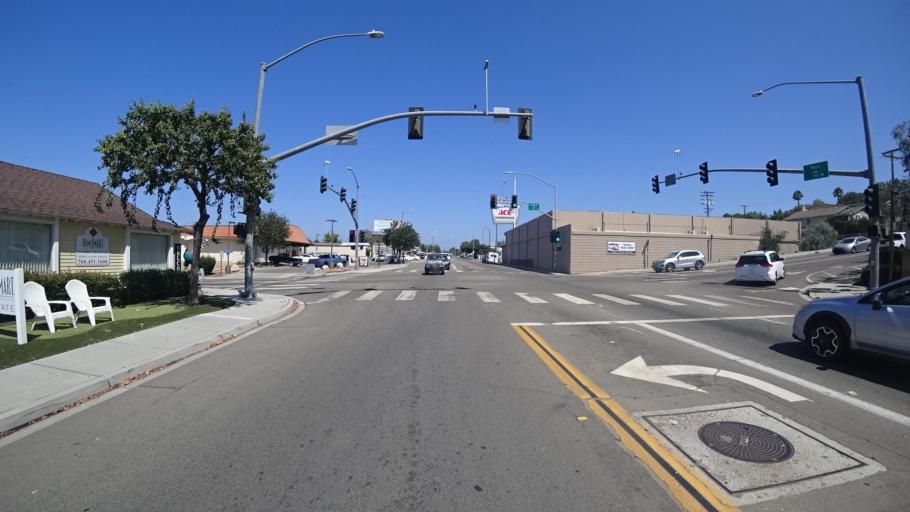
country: US
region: California
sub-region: San Diego County
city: Fallbrook
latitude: 33.3764
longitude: -117.2515
